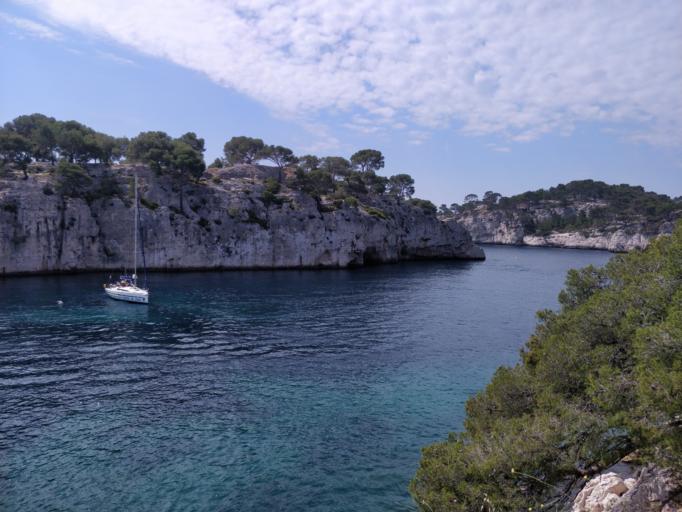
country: FR
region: Provence-Alpes-Cote d'Azur
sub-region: Departement des Bouches-du-Rhone
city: Cassis
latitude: 43.2058
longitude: 5.5149
